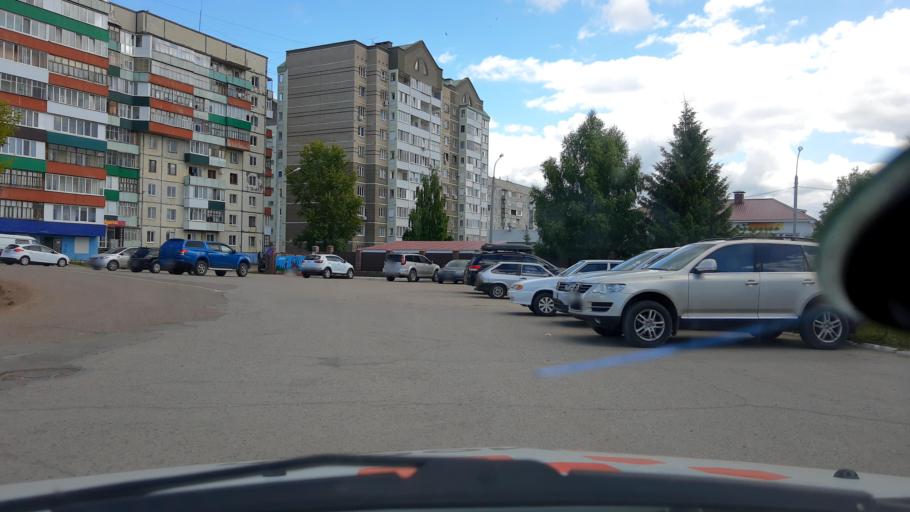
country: RU
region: Bashkortostan
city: Blagoveshchensk
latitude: 55.0480
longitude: 55.9601
